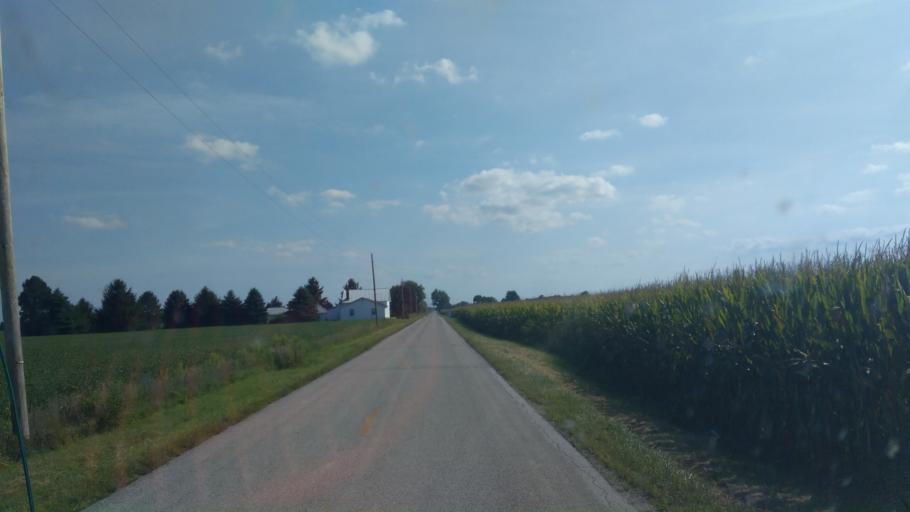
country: US
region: Ohio
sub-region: Hardin County
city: Forest
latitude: 40.7177
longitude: -83.5145
